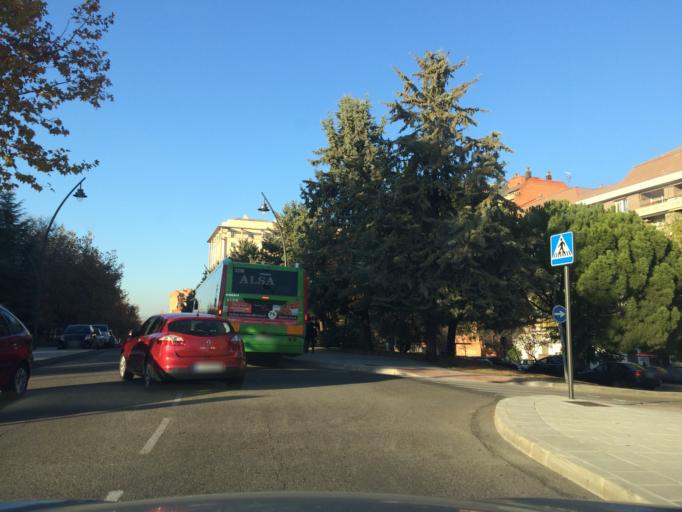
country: ES
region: Madrid
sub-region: Provincia de Madrid
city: Tres Cantos
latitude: 40.5936
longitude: -3.7031
